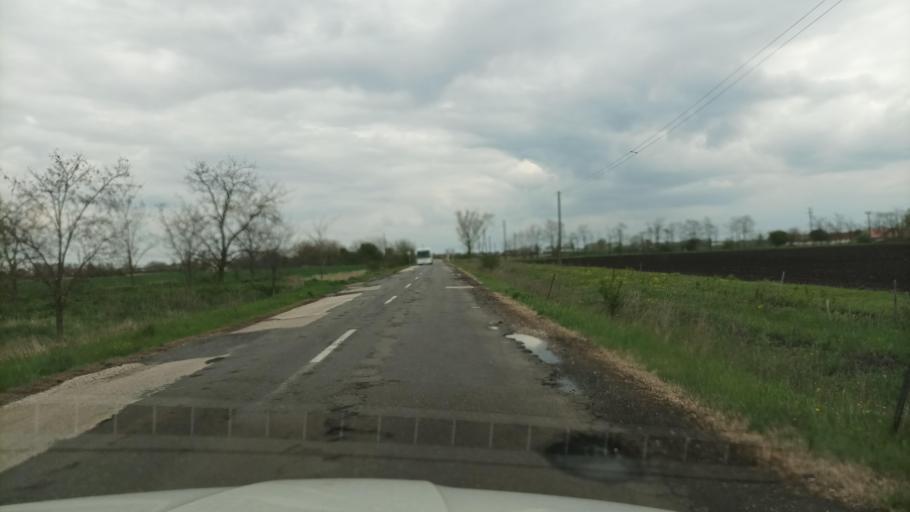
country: HU
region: Pest
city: Abony
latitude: 47.1721
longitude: 19.9840
